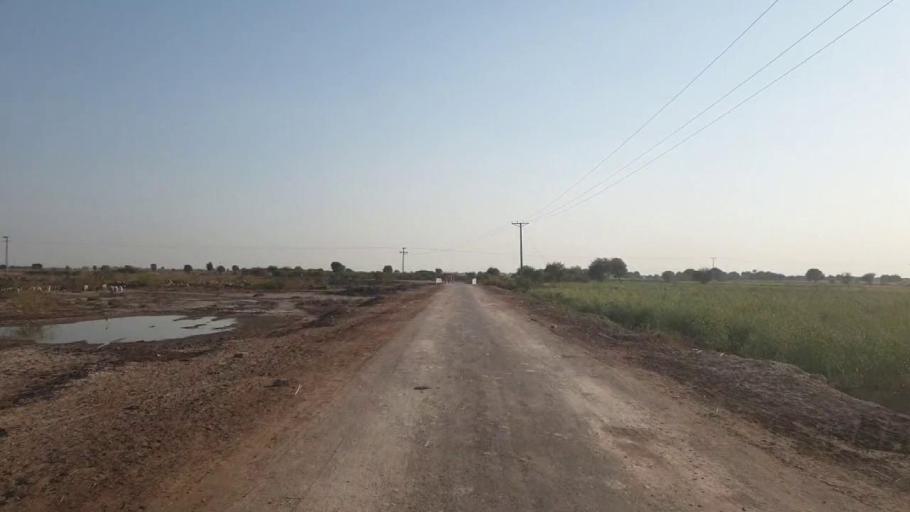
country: PK
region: Sindh
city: Chambar
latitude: 25.2837
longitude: 68.7498
